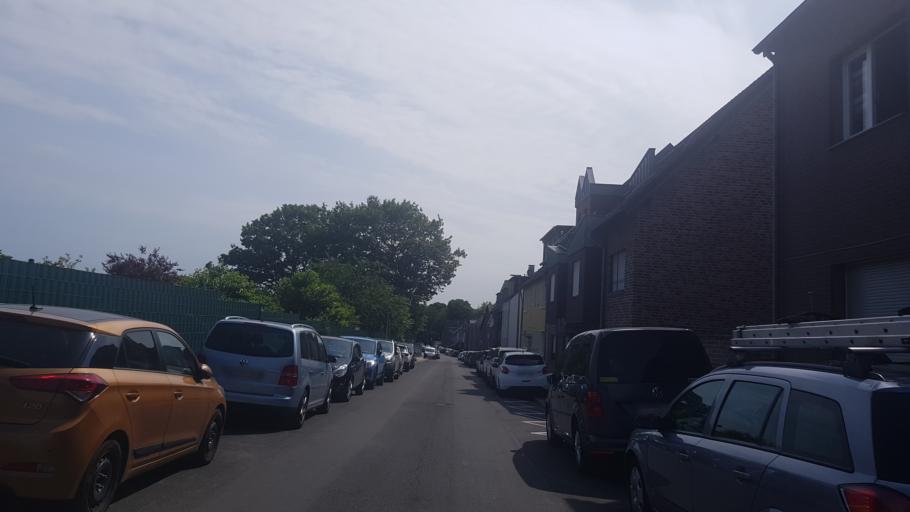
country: DE
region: North Rhine-Westphalia
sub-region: Regierungsbezirk Dusseldorf
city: Oberhausen
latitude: 51.4620
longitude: 6.8676
